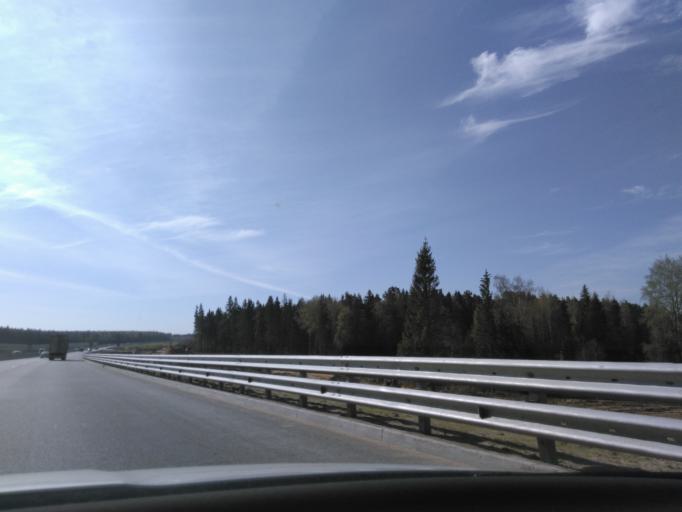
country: RU
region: Moskovskaya
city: Radumlya
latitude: 56.0918
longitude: 37.1966
